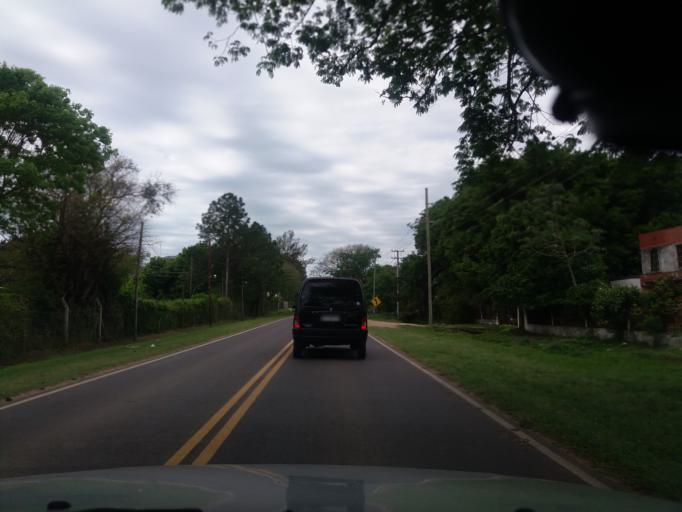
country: AR
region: Corrientes
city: Corrientes
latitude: -27.4508
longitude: -58.7359
